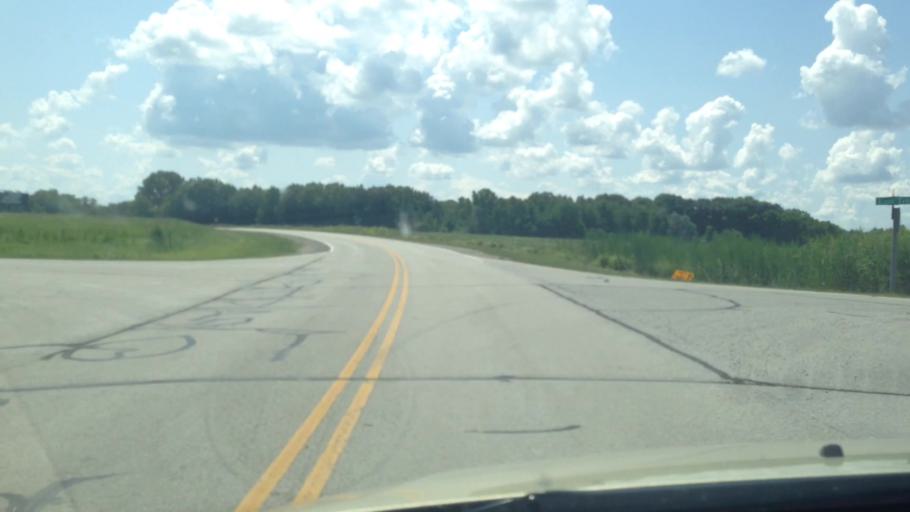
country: US
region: Wisconsin
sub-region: Brown County
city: Suamico
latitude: 44.6564
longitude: -88.0537
